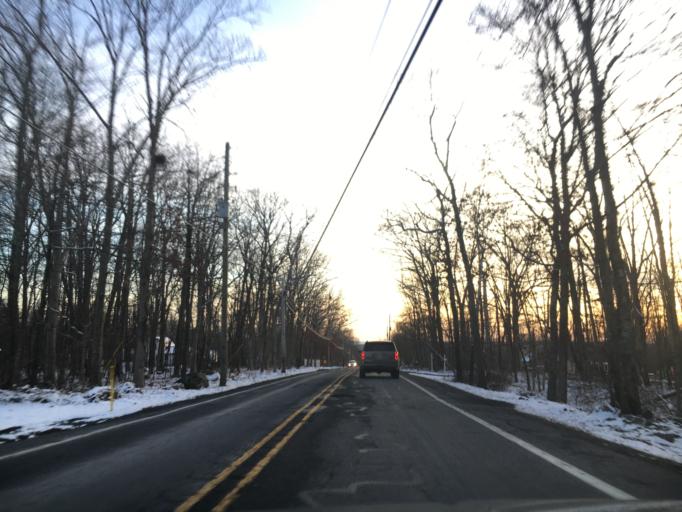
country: US
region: Pennsylvania
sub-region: Pike County
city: Saw Creek
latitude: 41.1261
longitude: -75.0903
